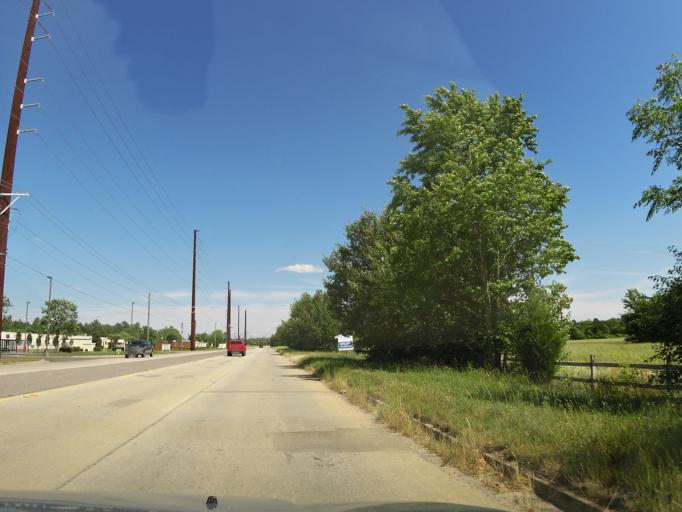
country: US
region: South Carolina
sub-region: Aiken County
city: Aiken
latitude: 33.5520
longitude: -81.6935
